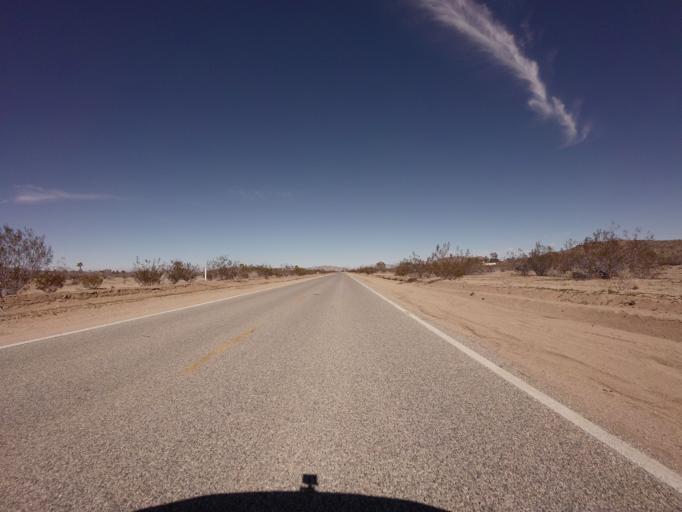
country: US
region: California
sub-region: San Bernardino County
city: Joshua Tree
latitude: 34.2501
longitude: -116.3932
